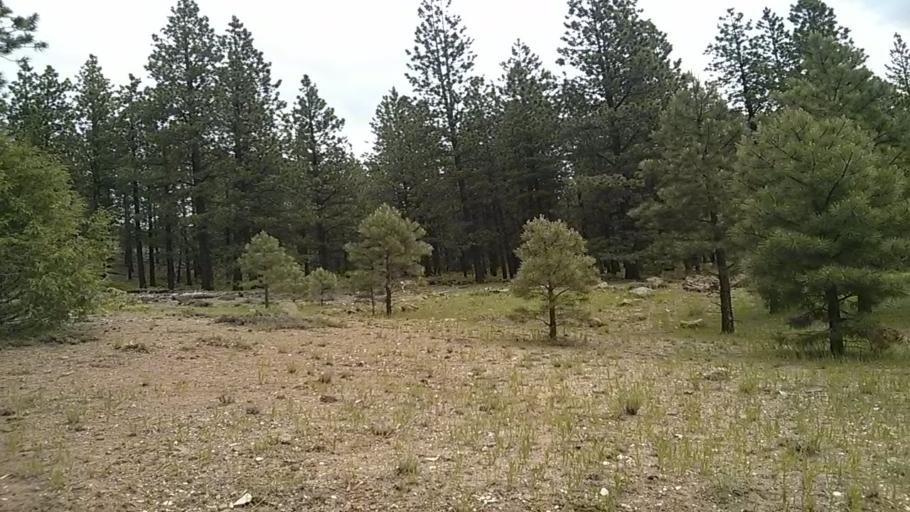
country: US
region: Utah
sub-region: Wayne County
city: Loa
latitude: 37.9454
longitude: -111.6587
